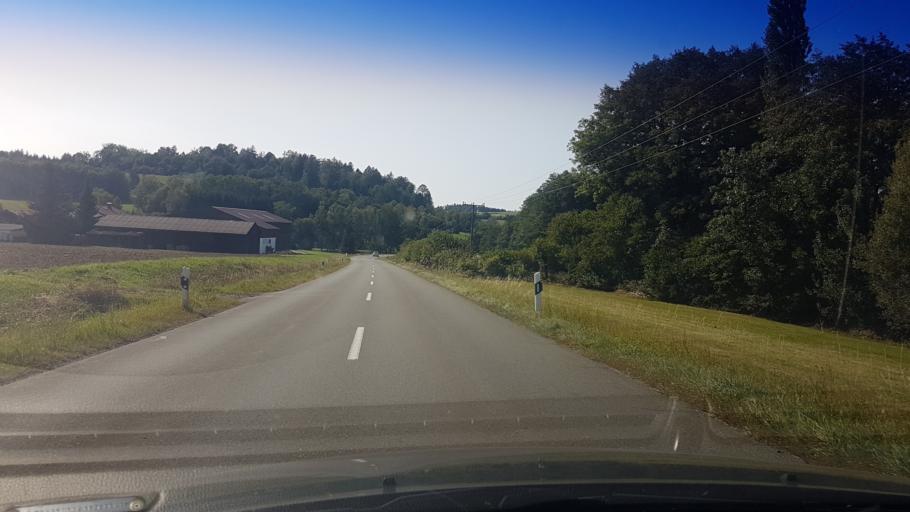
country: DE
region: Bavaria
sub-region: Upper Franconia
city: Marktschorgast
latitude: 50.0939
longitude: 11.6702
